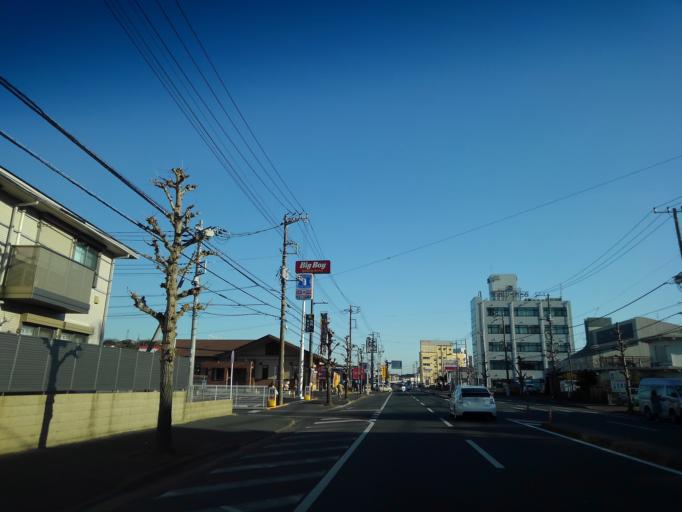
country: JP
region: Chiba
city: Kimitsu
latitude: 35.3351
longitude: 139.8967
